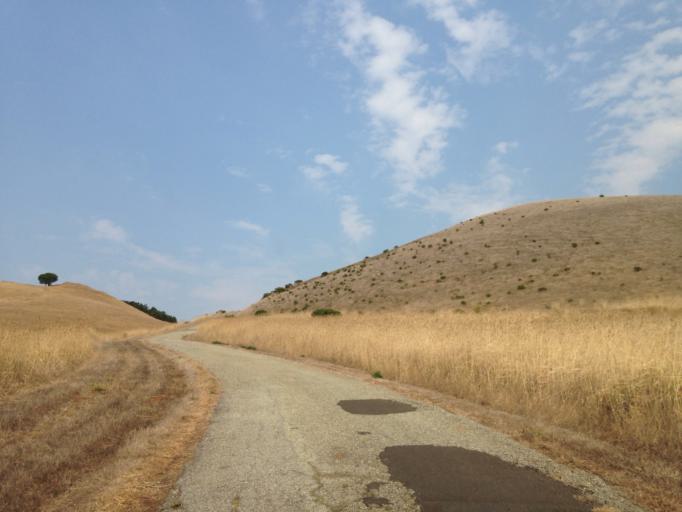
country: US
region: California
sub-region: San Mateo County
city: Portola Valley
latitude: 37.3689
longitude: -122.3011
